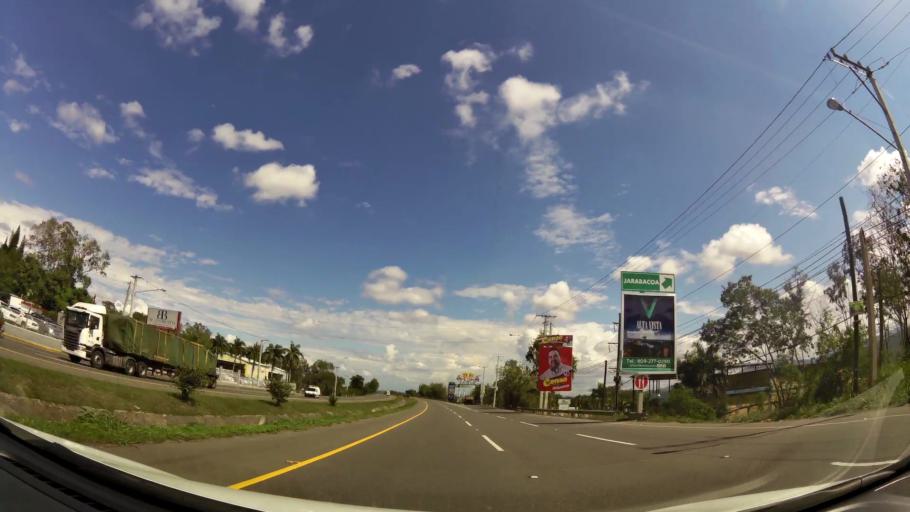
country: DO
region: La Vega
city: Concepcion de La Vega
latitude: 19.2516
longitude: -70.5584
